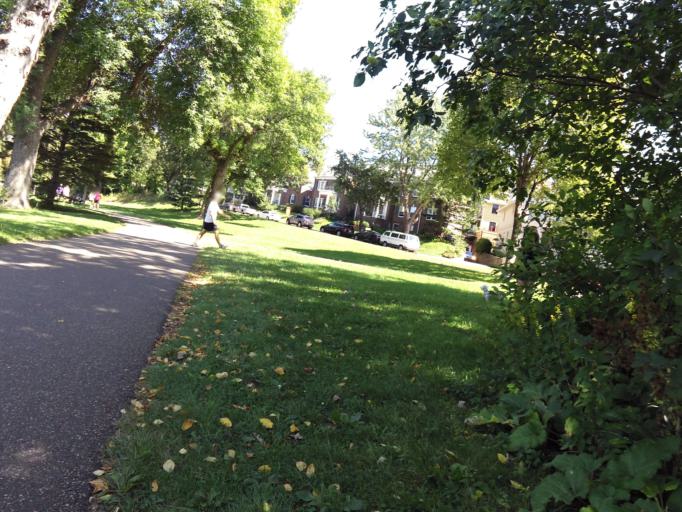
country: US
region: Minnesota
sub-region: Hennepin County
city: Saint Louis Park
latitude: 44.9516
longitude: -93.3048
